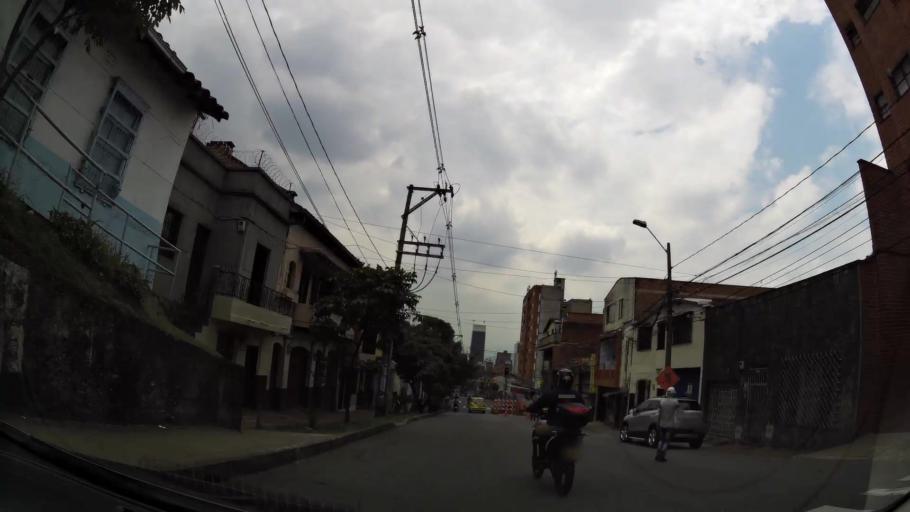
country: CO
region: Antioquia
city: Medellin
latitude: 6.2586
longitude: -75.5606
